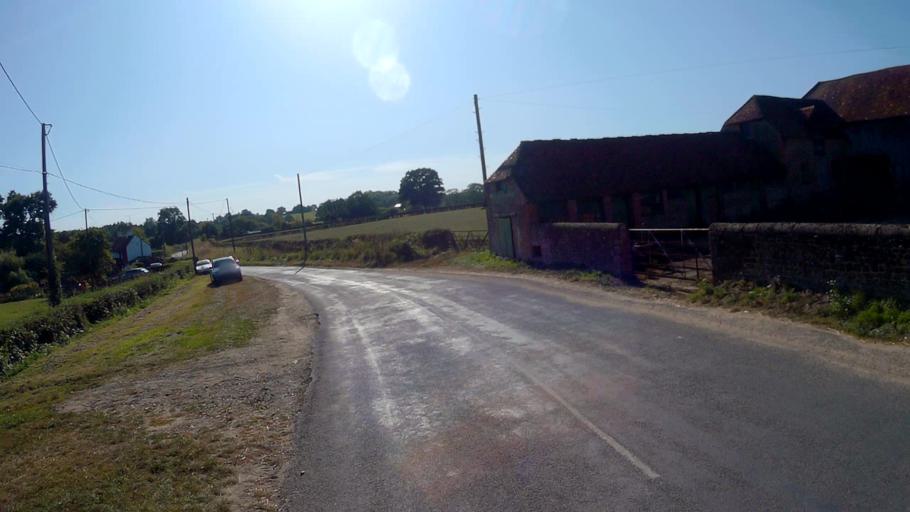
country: GB
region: England
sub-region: Surrey
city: Churt
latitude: 51.1633
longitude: -0.8056
